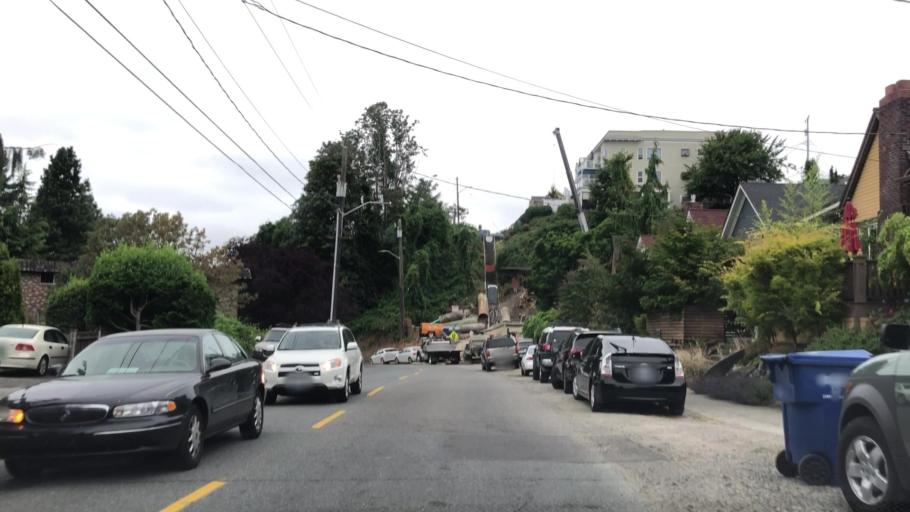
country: US
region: Washington
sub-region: King County
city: Seattle
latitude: 47.6361
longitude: -122.3715
